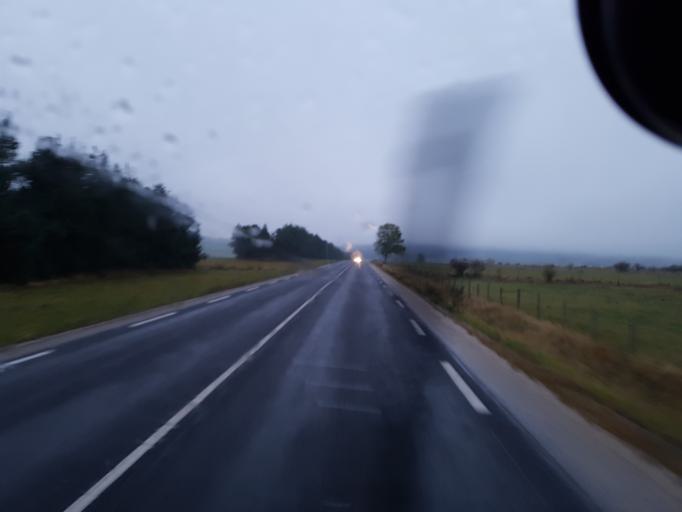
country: FR
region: Languedoc-Roussillon
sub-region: Departement de la Lozere
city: Langogne
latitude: 44.8109
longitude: 3.8795
